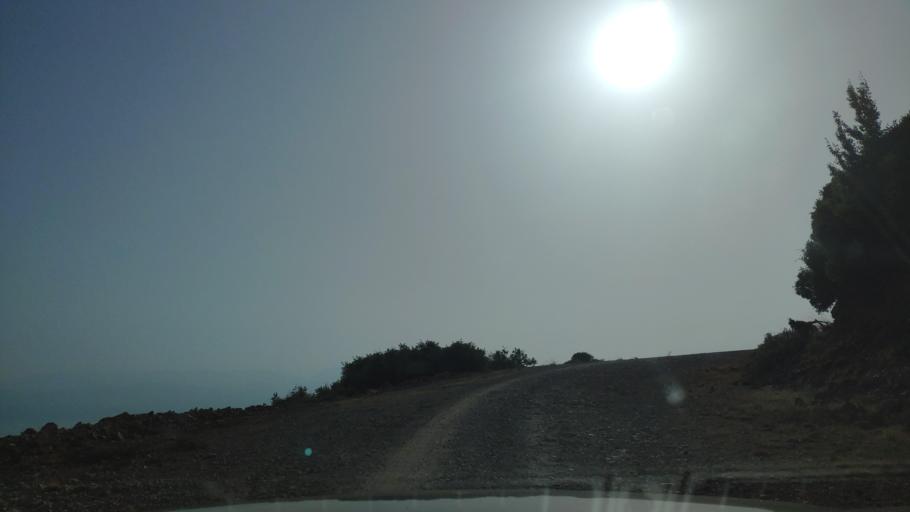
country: GR
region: West Greece
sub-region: Nomos Aitolias kai Akarnanias
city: Monastirakion
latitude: 38.8396
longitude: 20.9732
